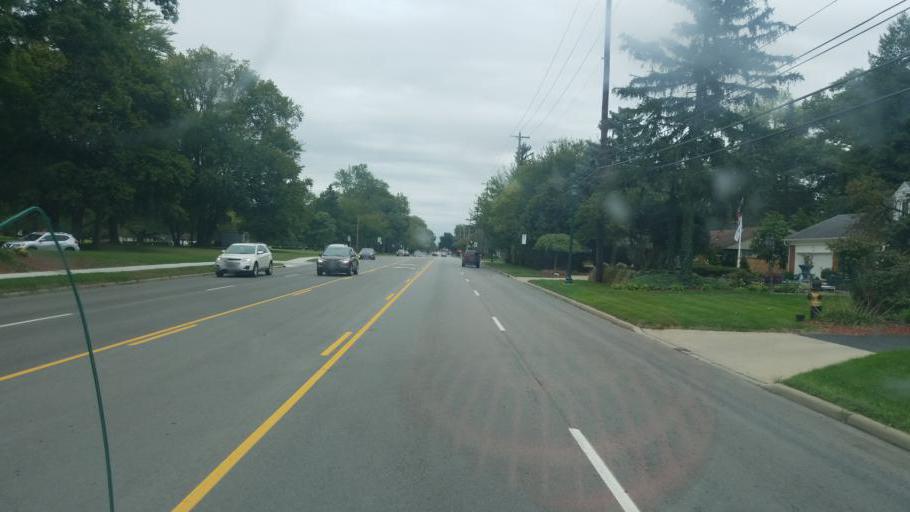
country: US
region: Ohio
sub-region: Lucas County
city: Ottawa Hills
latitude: 41.6770
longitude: -83.6412
